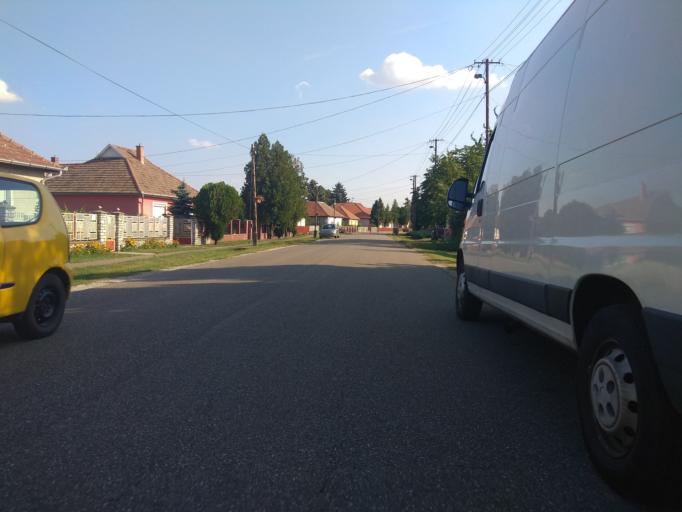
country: HU
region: Borsod-Abauj-Zemplen
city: Mezokeresztes
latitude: 47.8590
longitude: 20.6792
